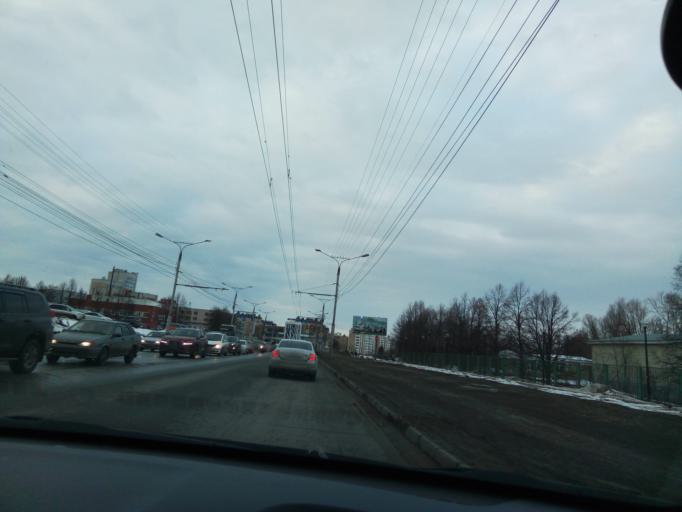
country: RU
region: Chuvashia
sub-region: Cheboksarskiy Rayon
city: Cheboksary
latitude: 56.1457
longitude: 47.2041
